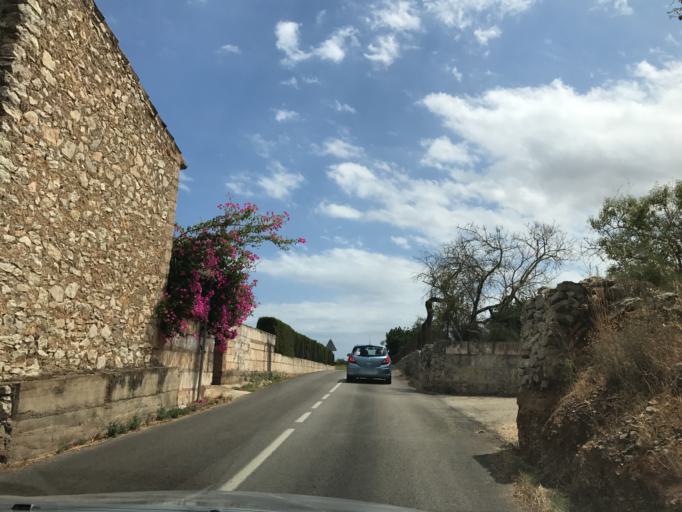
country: ES
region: Balearic Islands
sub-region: Illes Balears
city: Son Servera
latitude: 39.6461
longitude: 3.3458
